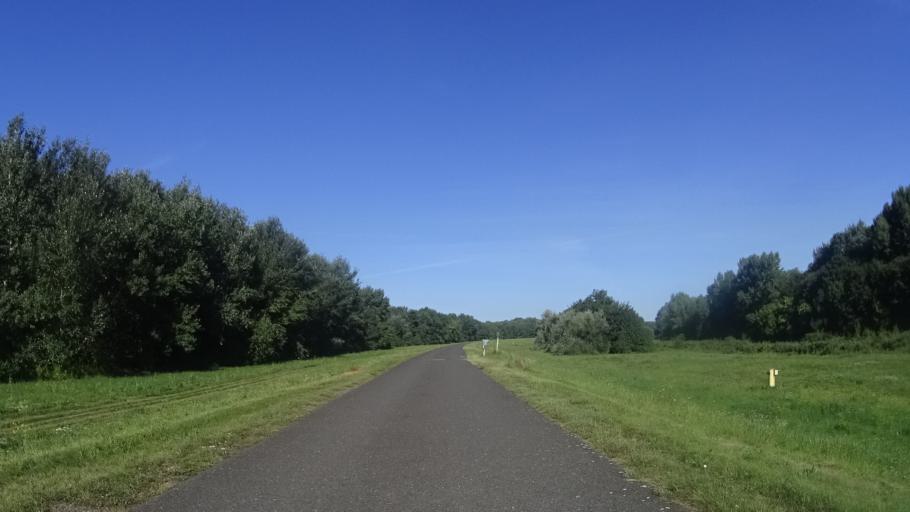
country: HU
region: Gyor-Moson-Sopron
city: Rajka
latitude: 48.0633
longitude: 17.1817
